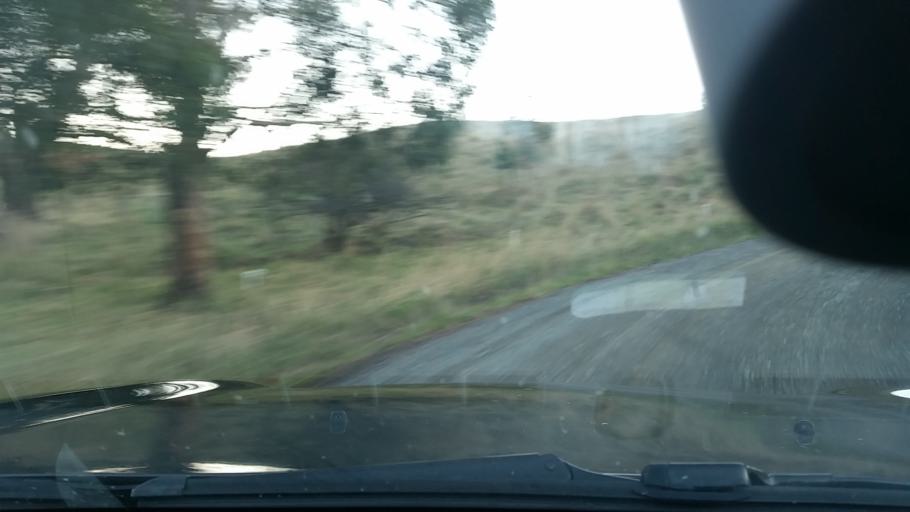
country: NZ
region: Marlborough
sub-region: Marlborough District
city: Blenheim
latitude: -41.7419
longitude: 174.0491
